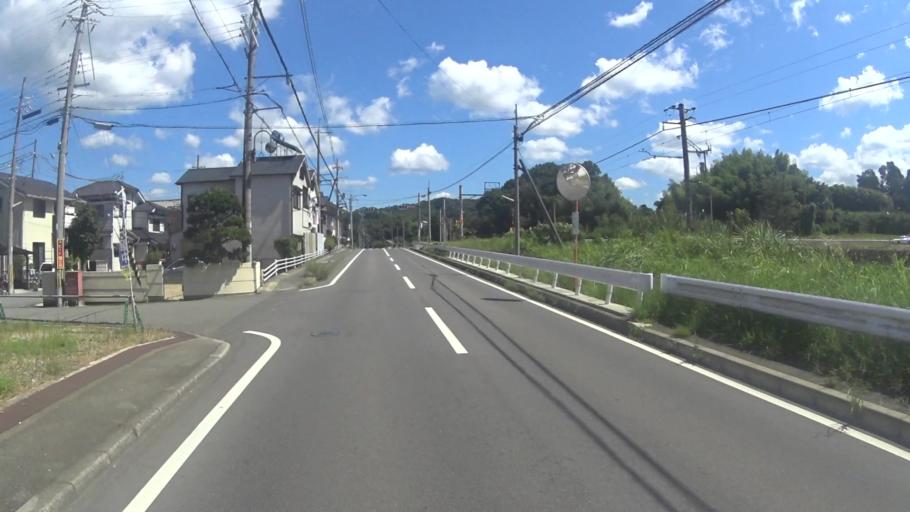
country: JP
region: Nara
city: Nara-shi
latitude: 34.7424
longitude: 135.8312
